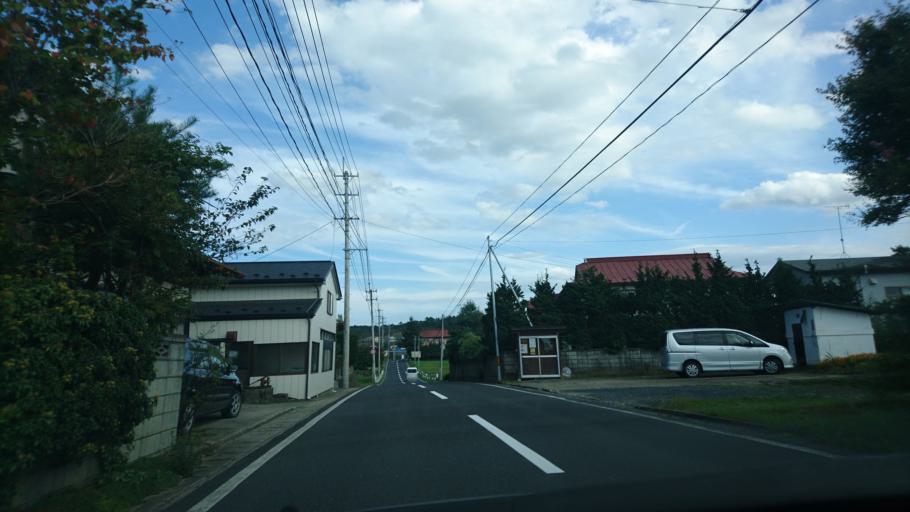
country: JP
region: Iwate
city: Ichinoseki
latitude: 38.8314
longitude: 141.1980
